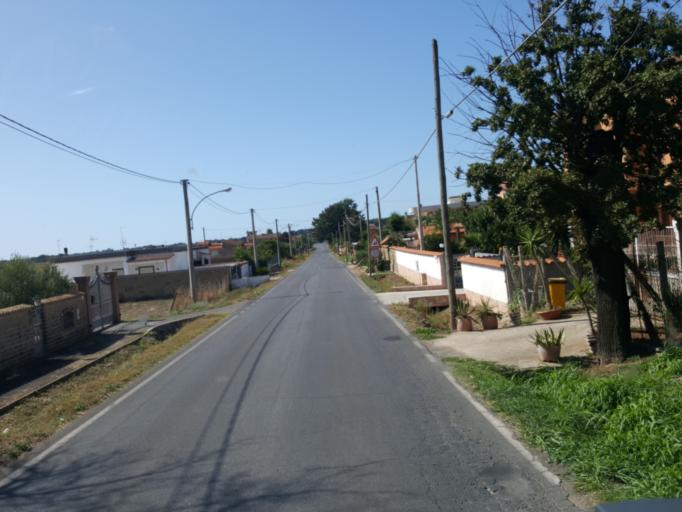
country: IT
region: Latium
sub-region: Citta metropolitana di Roma Capitale
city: Nettuno
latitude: 41.5015
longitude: 12.6845
